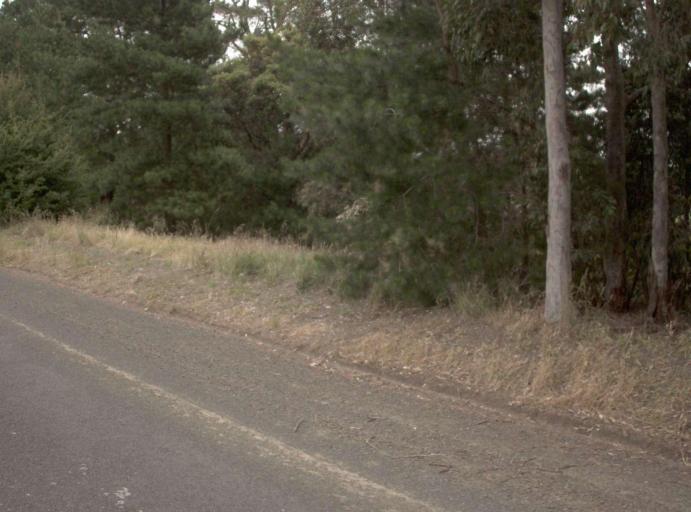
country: AU
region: Victoria
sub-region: Latrobe
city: Morwell
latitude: -38.2868
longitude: 146.3672
